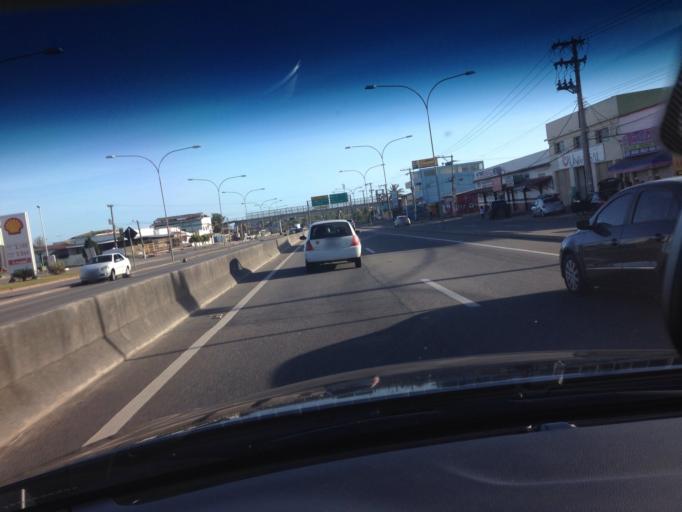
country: BR
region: Espirito Santo
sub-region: Viana
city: Viana
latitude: -20.5093
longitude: -40.3640
